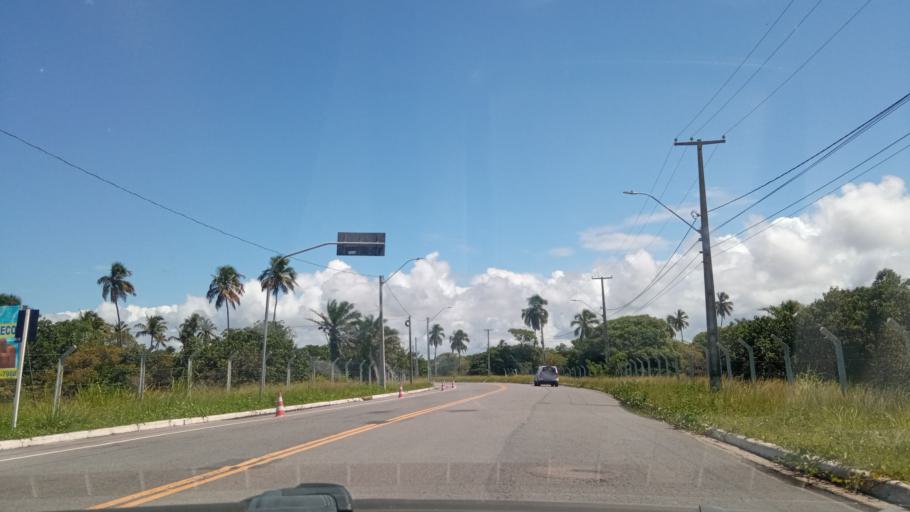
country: BR
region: Pernambuco
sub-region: Jaboatao Dos Guararapes
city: Jaboatao
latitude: -8.2294
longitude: -34.9339
